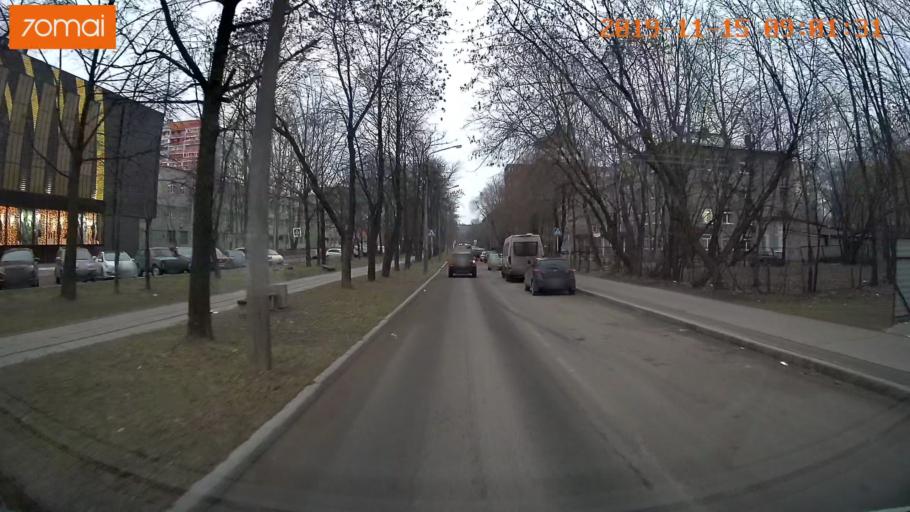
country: RU
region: Vologda
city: Cherepovets
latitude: 59.1326
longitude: 37.9260
